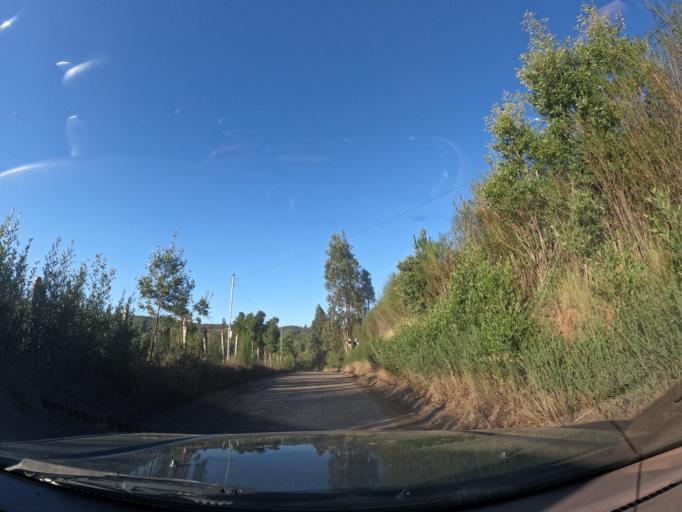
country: CL
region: Biobio
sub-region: Provincia de Concepcion
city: Chiguayante
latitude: -37.0306
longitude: -72.8779
